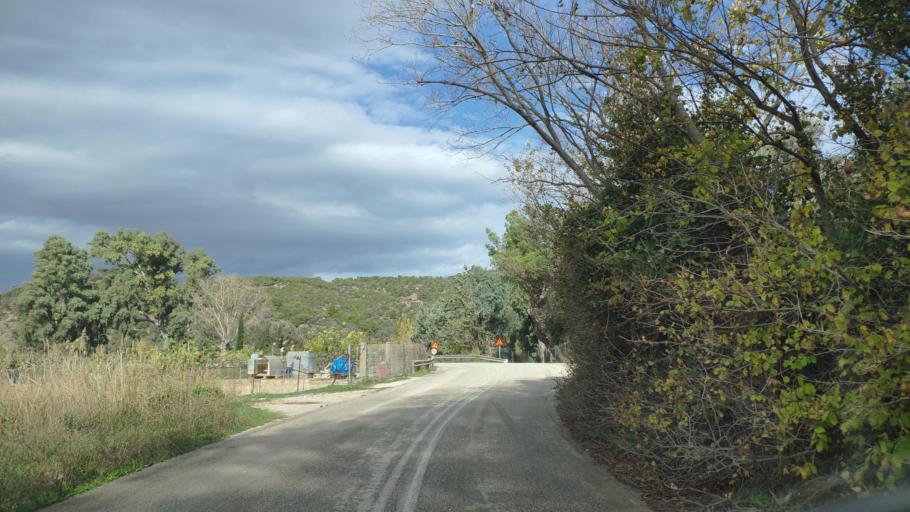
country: GR
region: Attica
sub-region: Nomarchia Anatolikis Attikis
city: Limin Mesoyaias
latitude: 37.9252
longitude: 23.9933
